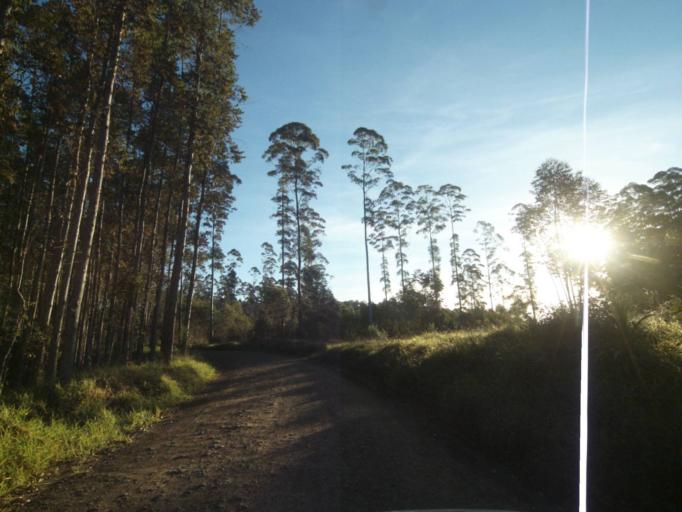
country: BR
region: Parana
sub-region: Telemaco Borba
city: Telemaco Borba
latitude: -24.4917
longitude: -50.5958
